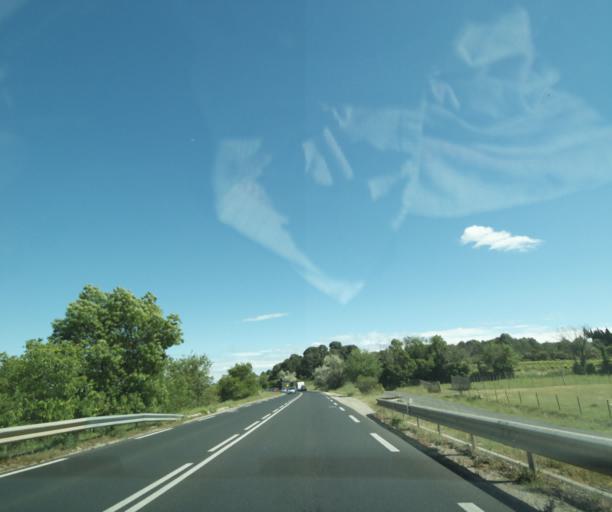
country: FR
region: Languedoc-Roussillon
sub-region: Departement de l'Herault
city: Saint-Jean-de-Vedas
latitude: 43.5866
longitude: 3.8361
